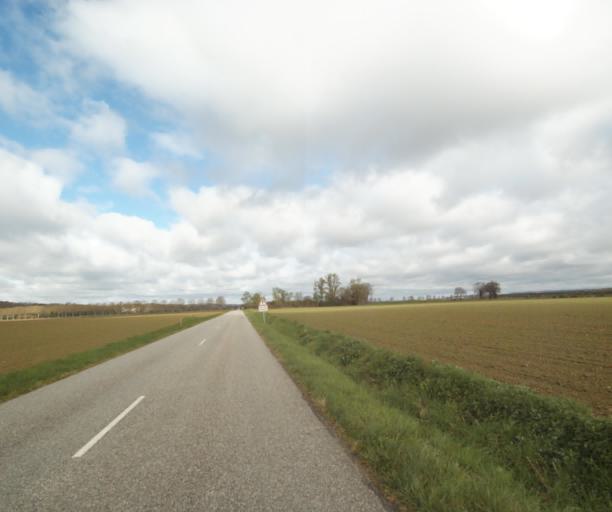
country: FR
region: Midi-Pyrenees
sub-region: Departement de l'Ariege
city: Saverdun
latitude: 43.2492
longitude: 1.5539
